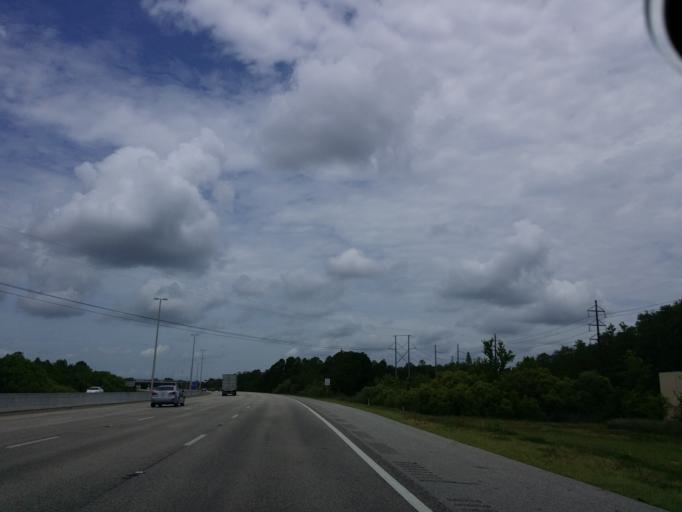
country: US
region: Florida
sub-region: Orange County
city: Tangelo Park
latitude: 28.4852
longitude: -81.4538
